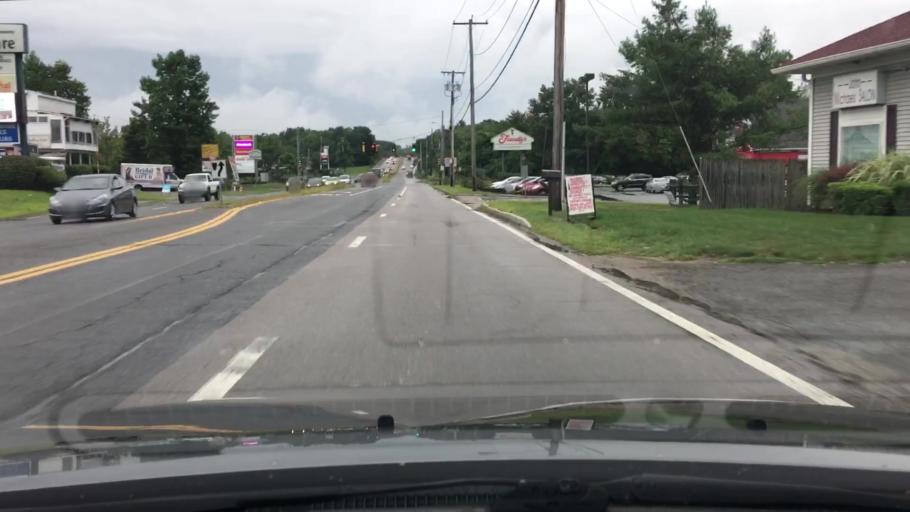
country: US
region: Rhode Island
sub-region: Providence County
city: Valley Falls
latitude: 41.9301
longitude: -71.3533
